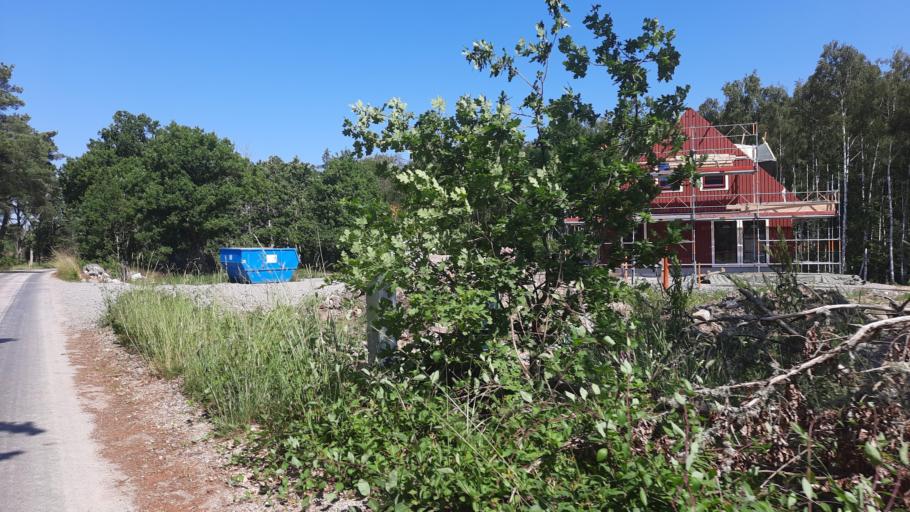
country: SE
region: Blekinge
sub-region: Karlskrona Kommun
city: Jaemjoe
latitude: 56.1484
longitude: 15.7698
